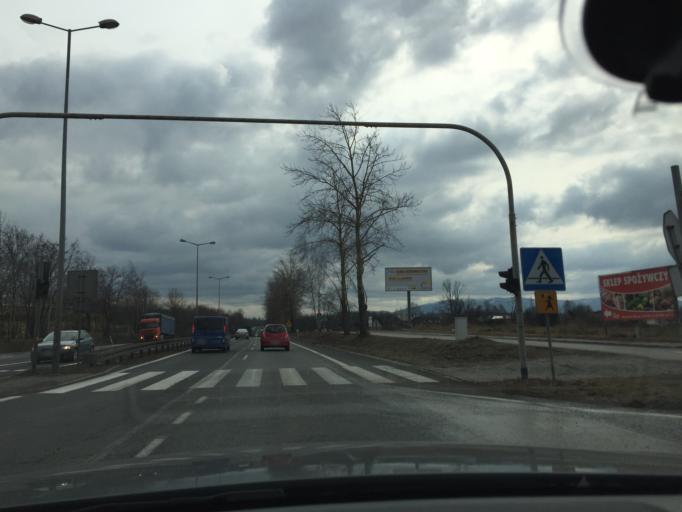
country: PL
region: Silesian Voivodeship
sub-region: Powiat bielski
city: Czechowice-Dziedzice
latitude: 49.8923
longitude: 18.9935
